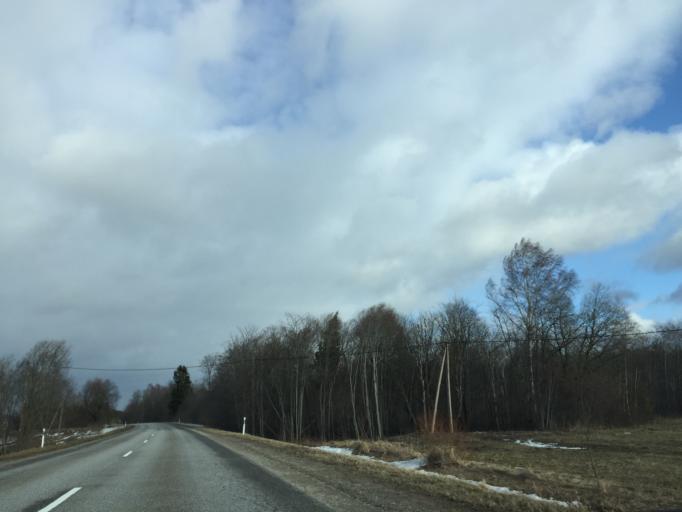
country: LV
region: Aloja
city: Staicele
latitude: 57.8832
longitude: 24.6022
